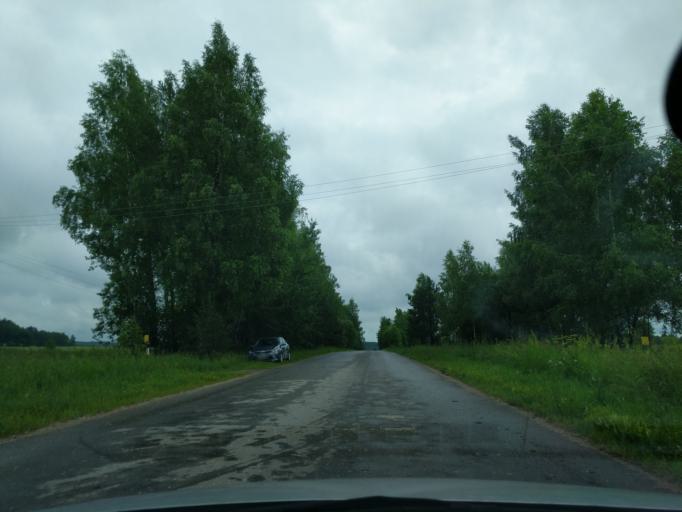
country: RU
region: Kaluga
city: Myatlevo
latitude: 54.8205
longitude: 35.6740
